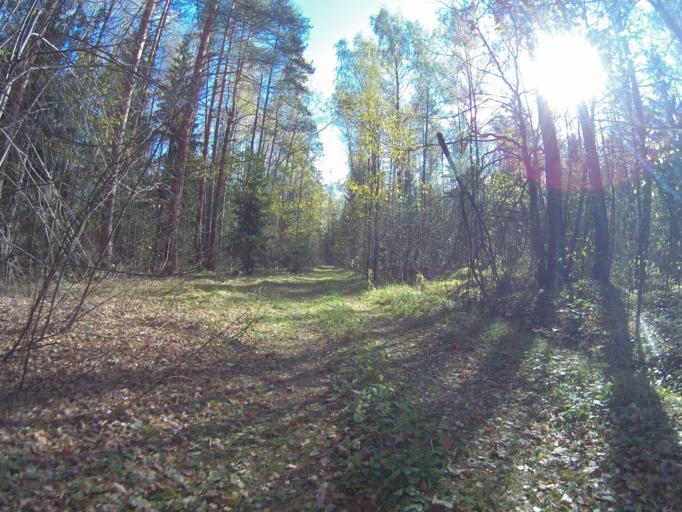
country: RU
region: Vladimir
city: Golovino
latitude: 56.0174
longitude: 40.4784
